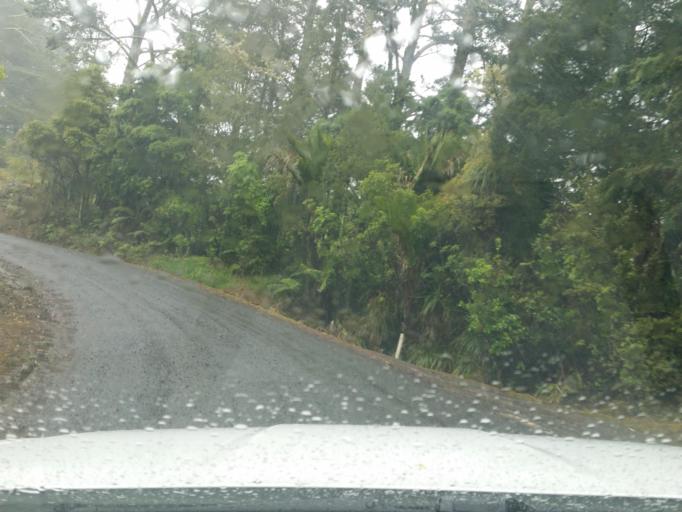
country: NZ
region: Northland
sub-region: Kaipara District
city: Dargaville
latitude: -35.7617
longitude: 173.9668
